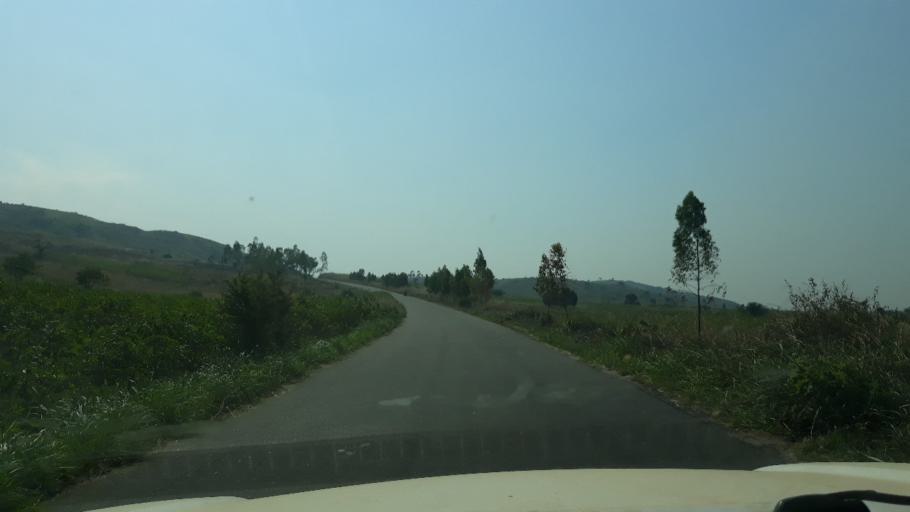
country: CD
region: South Kivu
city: Uvira
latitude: -3.2070
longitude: 29.1634
